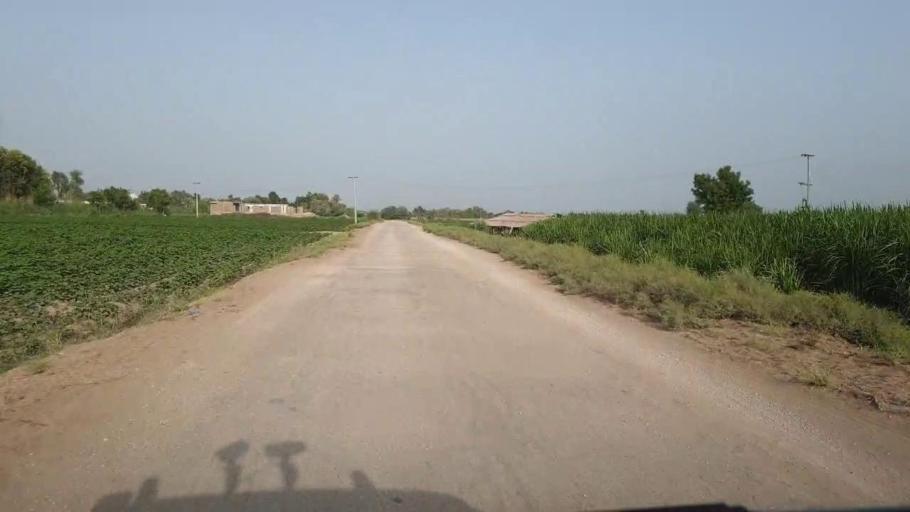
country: PK
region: Sindh
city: Daur
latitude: 26.3428
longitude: 68.2819
